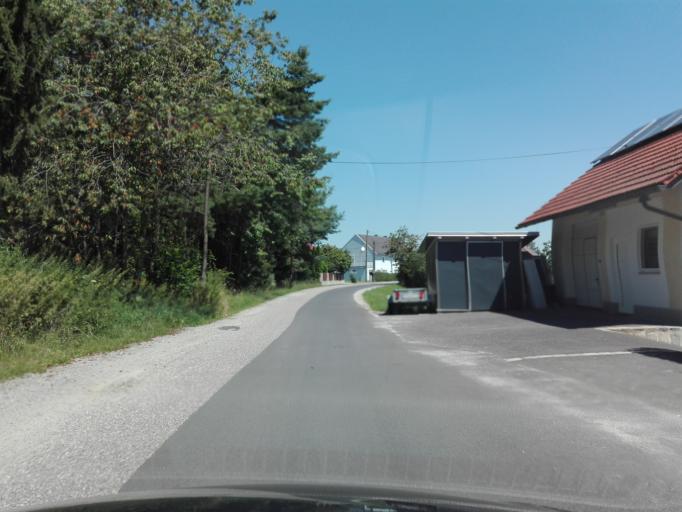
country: AT
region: Upper Austria
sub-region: Politischer Bezirk Urfahr-Umgebung
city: Steyregg
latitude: 48.3285
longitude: 14.3769
